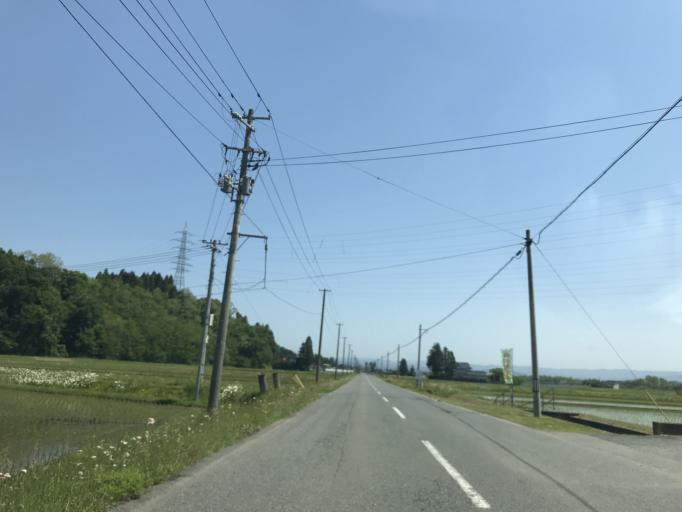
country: JP
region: Iwate
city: Mizusawa
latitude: 39.1628
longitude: 141.0779
